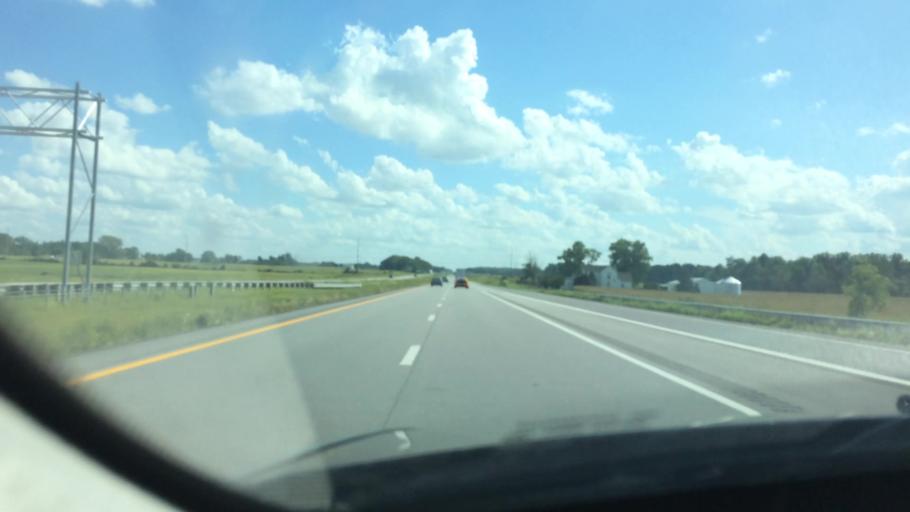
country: US
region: Ohio
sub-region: Auglaize County
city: Wapakoneta
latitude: 40.5520
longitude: -84.1700
